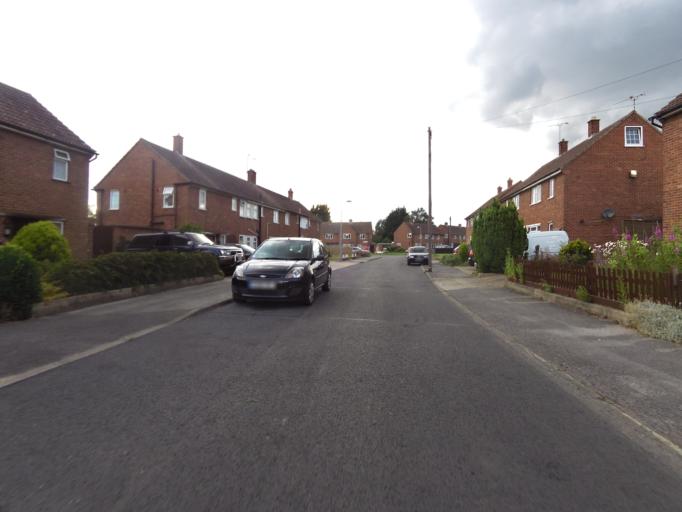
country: GB
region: England
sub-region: Suffolk
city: Bramford
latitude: 52.0763
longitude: 1.1180
